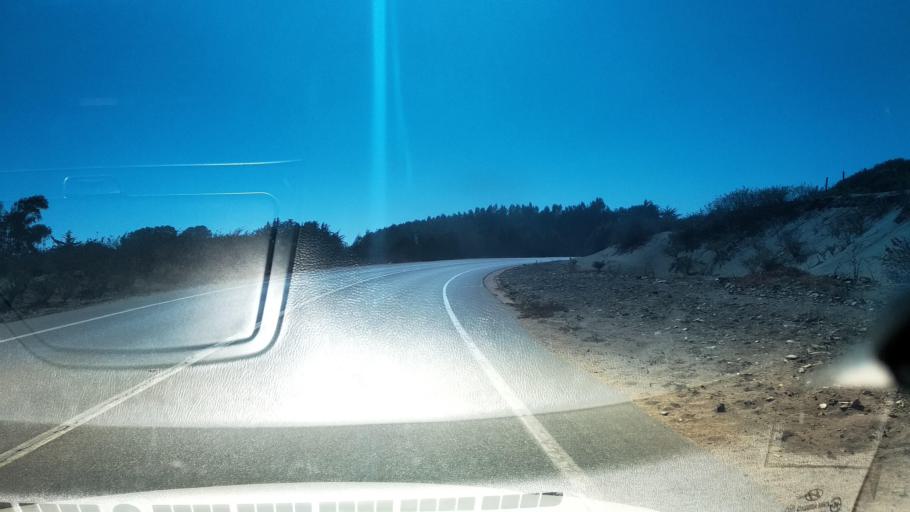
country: CL
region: O'Higgins
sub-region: Provincia de Colchagua
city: Santa Cruz
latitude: -34.4744
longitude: -72.0181
